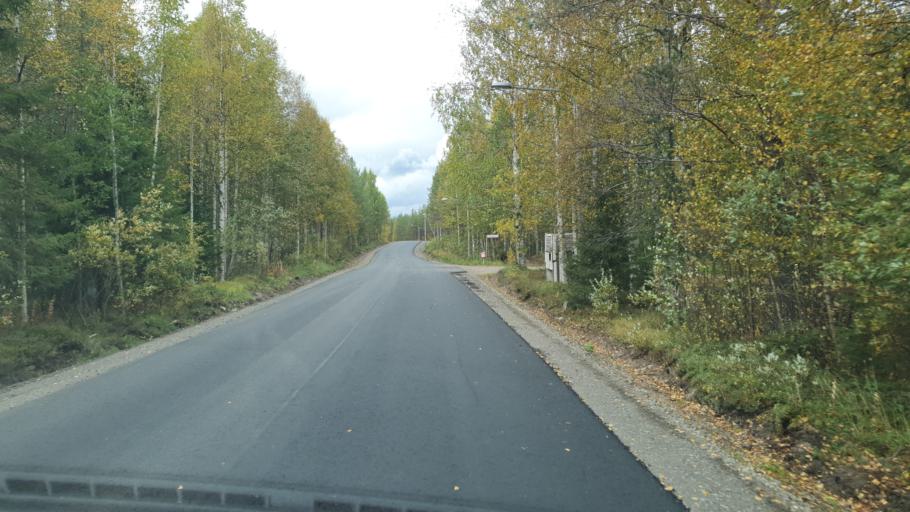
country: FI
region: Lapland
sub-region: Rovaniemi
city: Rovaniemi
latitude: 66.4224
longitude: 25.4041
